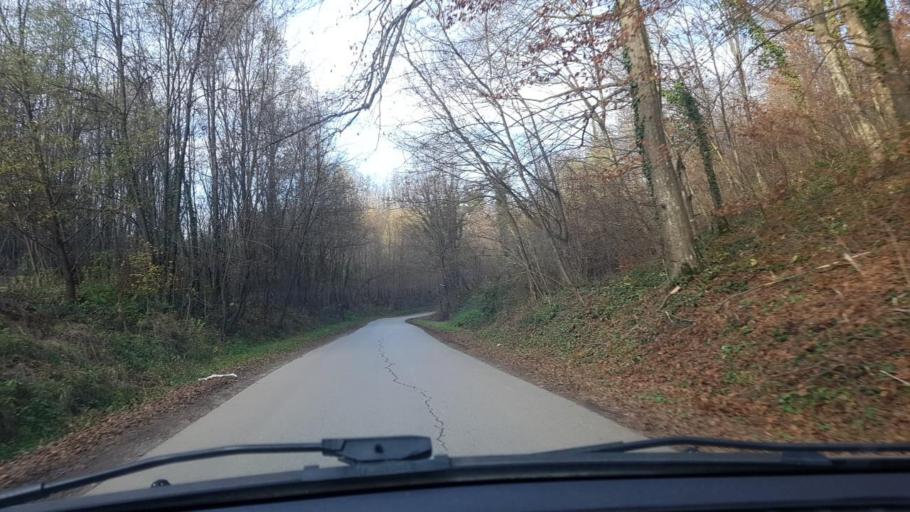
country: HR
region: Krapinsko-Zagorska
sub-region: Grad Krapina
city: Krapina
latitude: 46.1310
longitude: 15.8720
